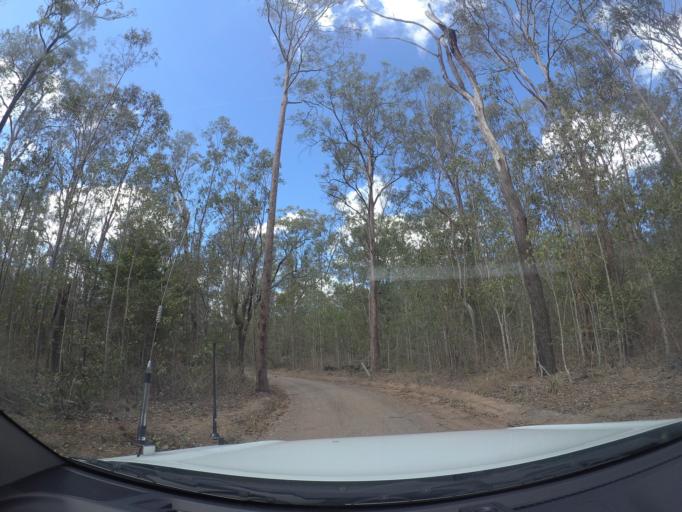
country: AU
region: Queensland
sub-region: Logan
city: North Maclean
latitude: -27.8285
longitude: 152.9680
